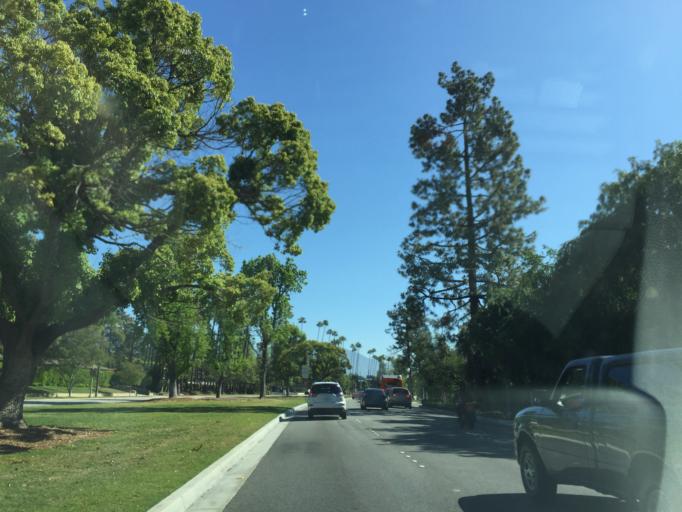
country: US
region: California
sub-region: Los Angeles County
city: San Marino
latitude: 34.1165
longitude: -118.1197
